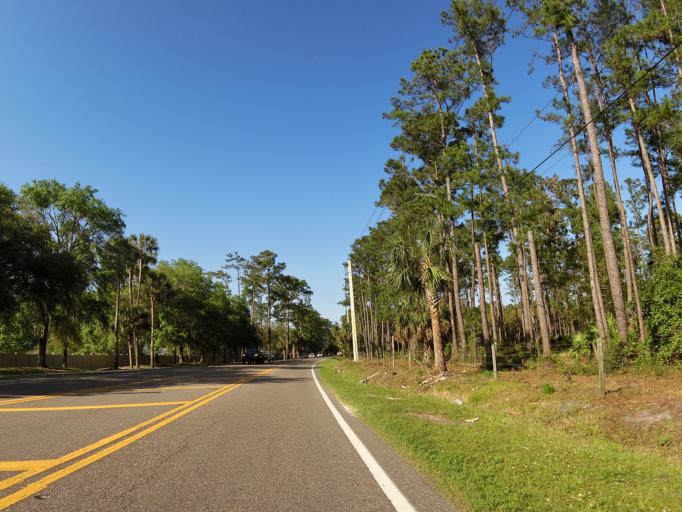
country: US
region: Florida
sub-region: Saint Johns County
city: Palm Valley
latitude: 30.1374
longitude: -81.3805
